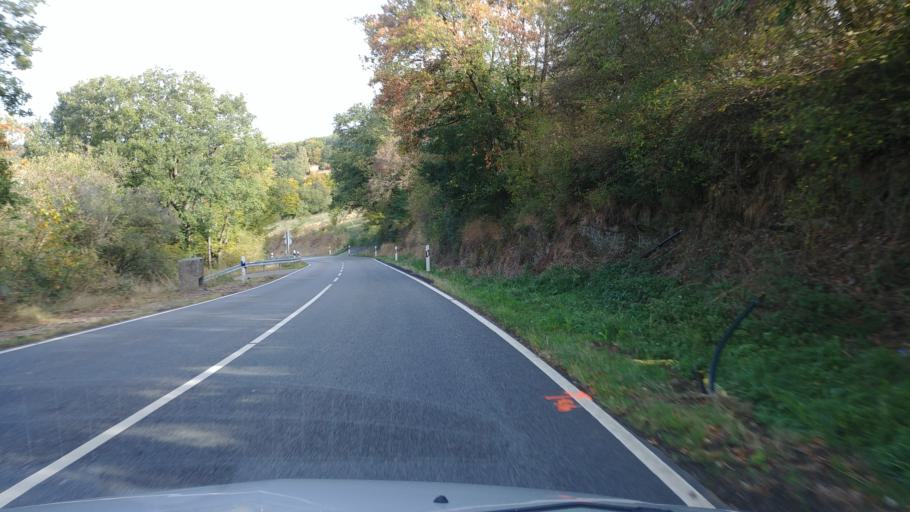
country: DE
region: Rheinland-Pfalz
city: Reckenroth
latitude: 50.2089
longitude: 8.0006
